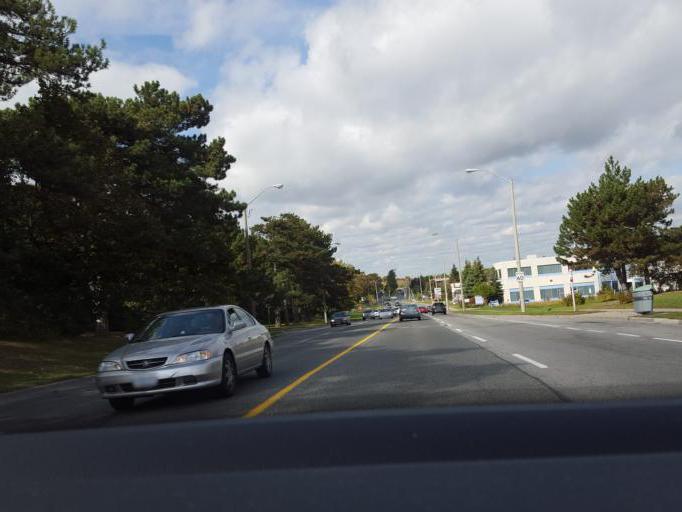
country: CA
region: Ontario
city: Scarborough
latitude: 43.8052
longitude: -79.2008
